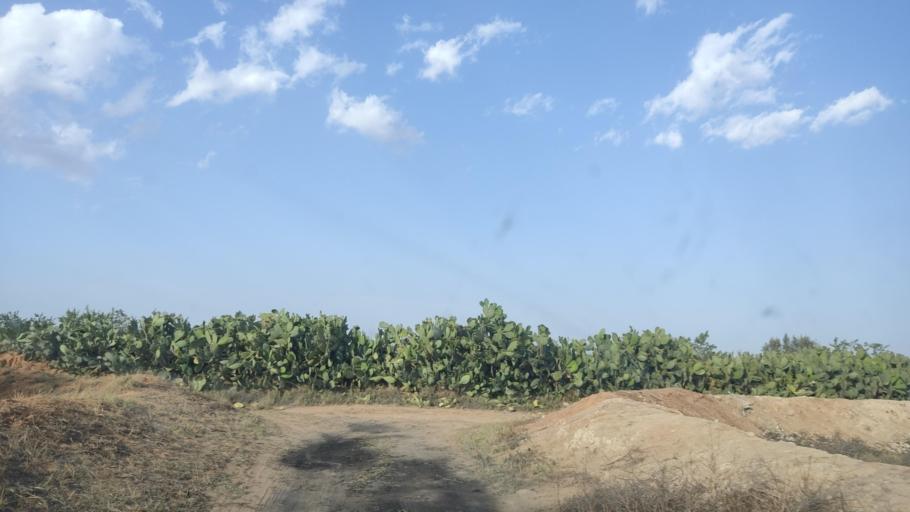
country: TN
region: Safaqis
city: Sfax
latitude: 34.8491
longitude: 10.5939
